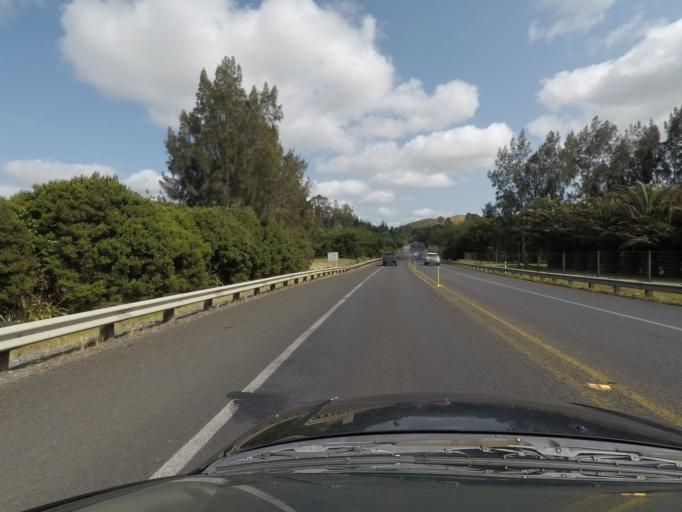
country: NZ
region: Northland
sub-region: Whangarei
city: Whangarei
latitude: -35.8296
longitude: 174.3132
